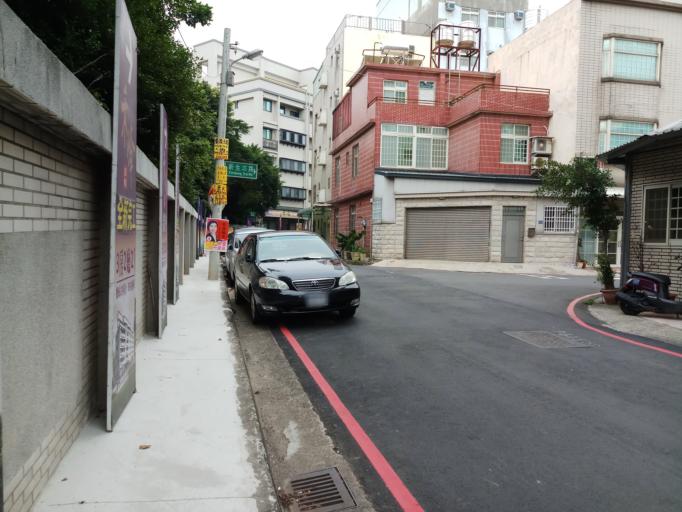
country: TW
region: Taiwan
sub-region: Hsinchu
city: Zhubei
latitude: 24.8674
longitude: 121.0269
